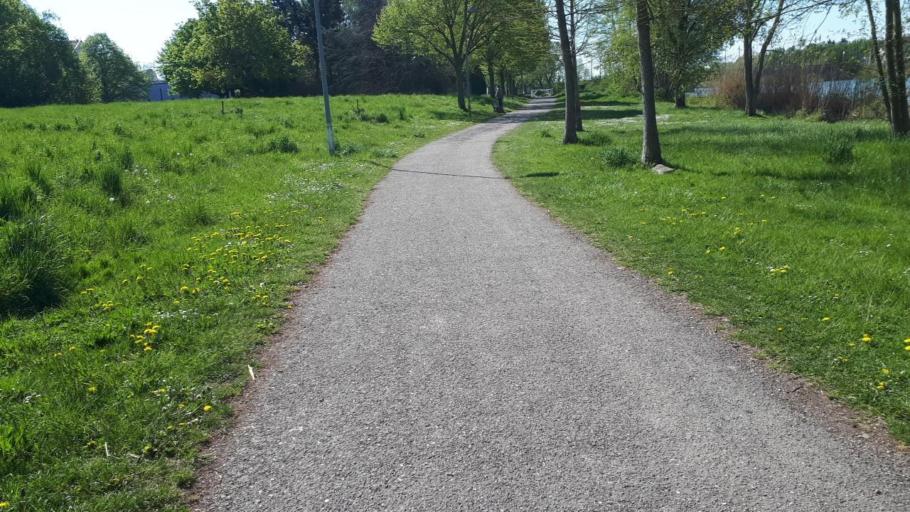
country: FR
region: Lorraine
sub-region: Departement de Meurthe-et-Moselle
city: Tomblaine
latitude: 48.6901
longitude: 6.2067
